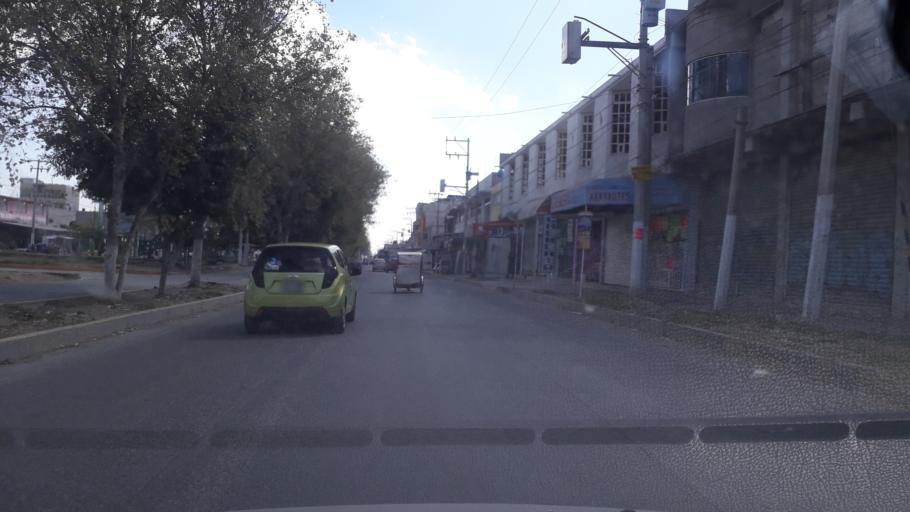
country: MX
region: Mexico
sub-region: Jaltenco
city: Alborada Jaltenco
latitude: 19.6493
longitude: -99.0638
